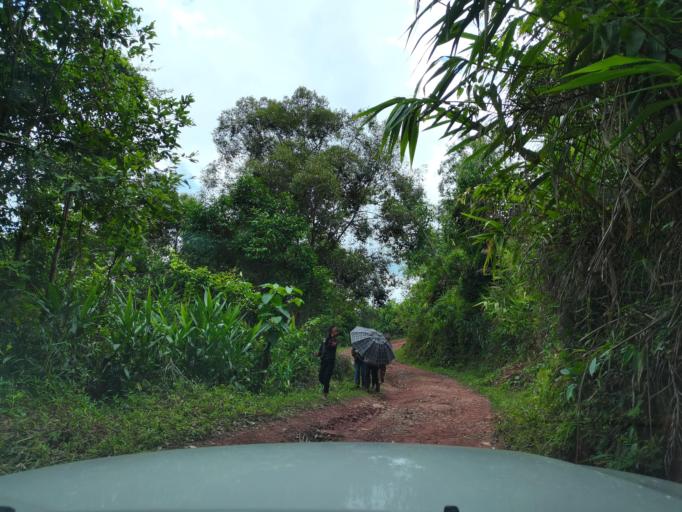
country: LA
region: Loungnamtha
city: Muang Nale
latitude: 20.5060
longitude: 101.0843
